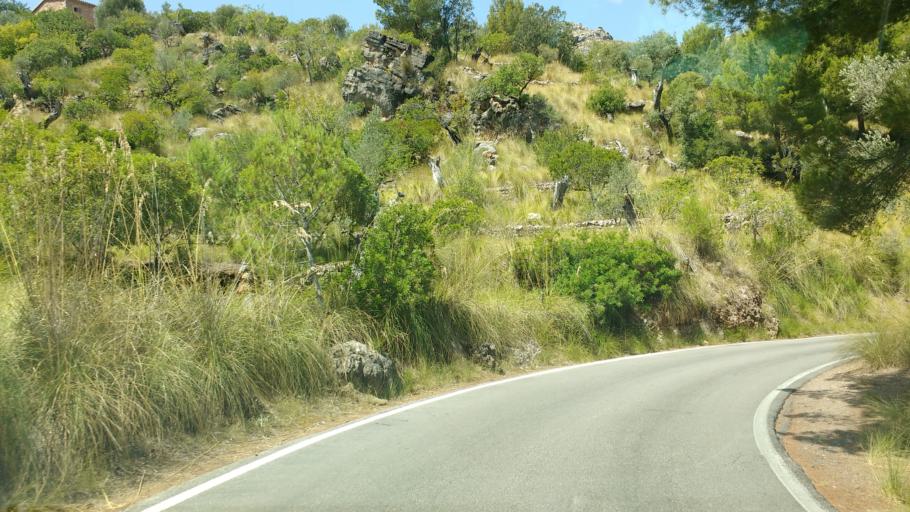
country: ES
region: Balearic Islands
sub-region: Illes Balears
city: Escorca
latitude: 39.8430
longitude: 2.7955
